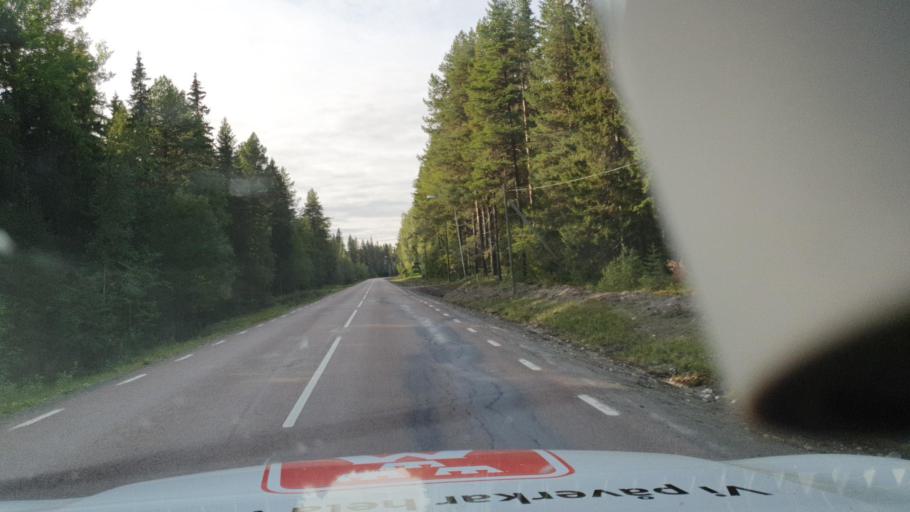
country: SE
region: Jaemtland
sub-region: Stroemsunds Kommun
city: Stroemsund
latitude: 63.7239
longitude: 15.7940
